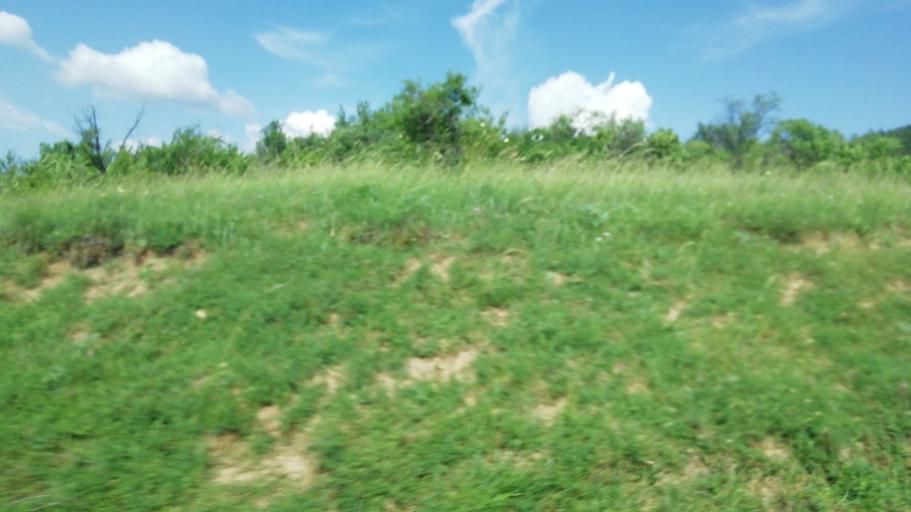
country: TR
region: Karabuk
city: Karabuk
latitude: 41.1256
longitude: 32.5753
